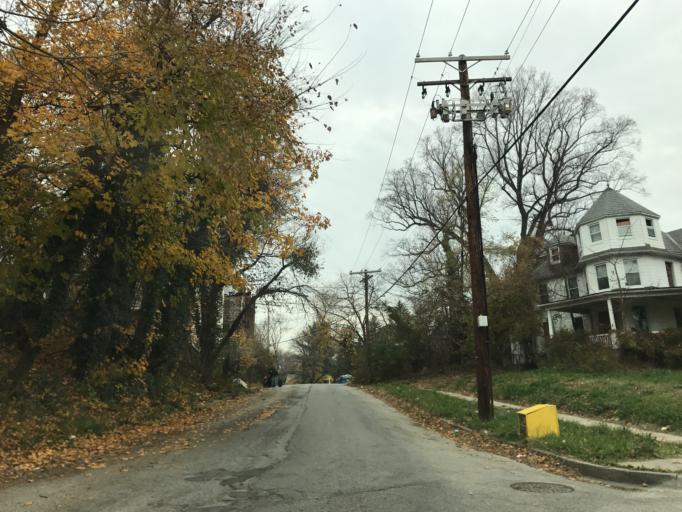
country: US
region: Maryland
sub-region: Baltimore County
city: Woodlawn
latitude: 39.3129
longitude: -76.6809
